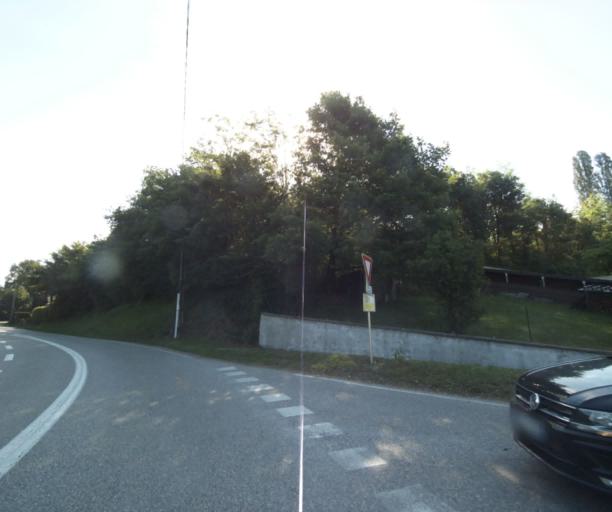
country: FR
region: Rhone-Alpes
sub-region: Departement de la Haute-Savoie
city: Thonon-les-Bains
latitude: 46.3591
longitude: 6.4965
